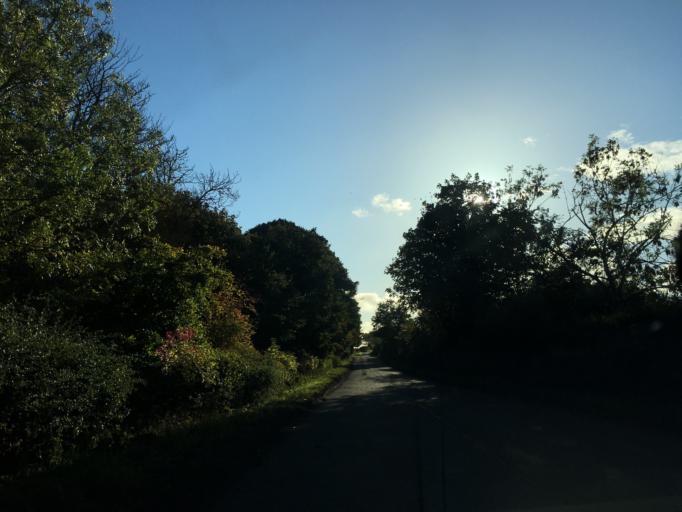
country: GB
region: Scotland
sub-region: East Lothian
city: Pencaitland
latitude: 55.8668
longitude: -2.9014
